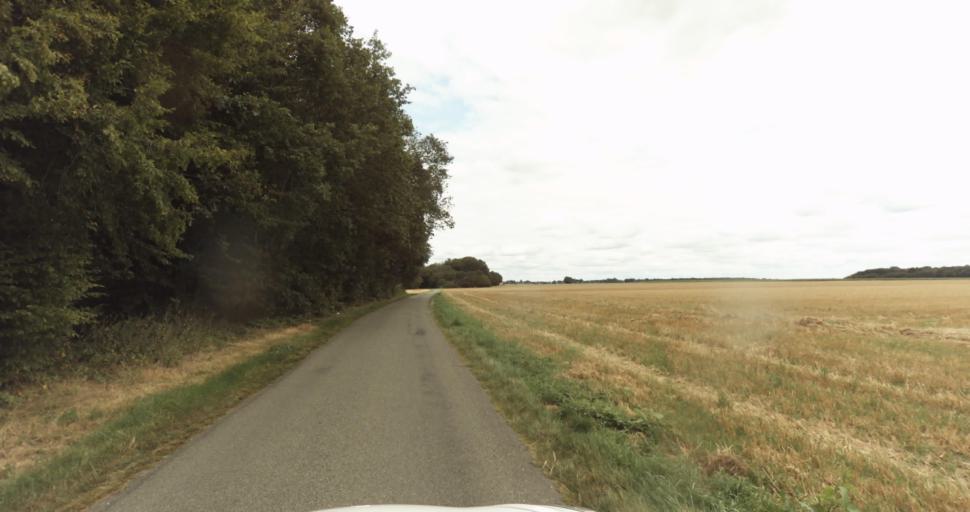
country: FR
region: Haute-Normandie
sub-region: Departement de l'Eure
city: Saint-Germain-sur-Avre
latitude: 48.8112
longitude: 1.2551
